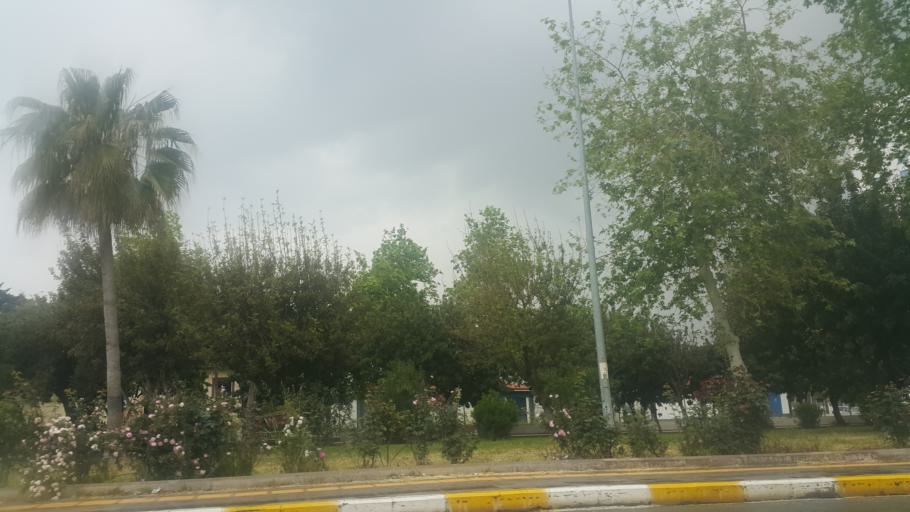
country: TR
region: Mersin
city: Mercin
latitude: 36.8026
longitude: 34.6368
